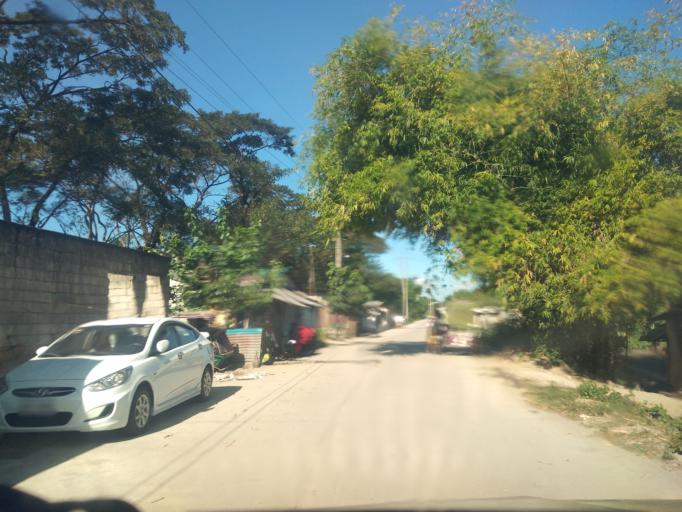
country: PH
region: Central Luzon
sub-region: Province of Pampanga
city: Calibutbut
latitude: 15.0876
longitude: 120.6024
